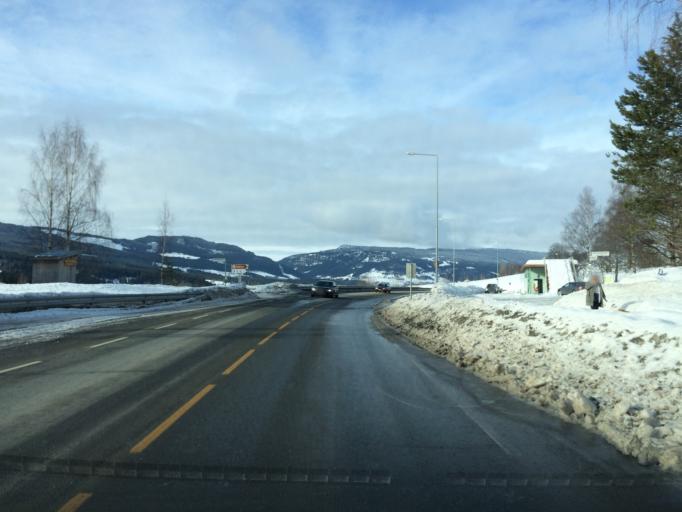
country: NO
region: Oppland
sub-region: Gausdal
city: Segalstad bru
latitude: 61.2191
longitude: 10.2730
